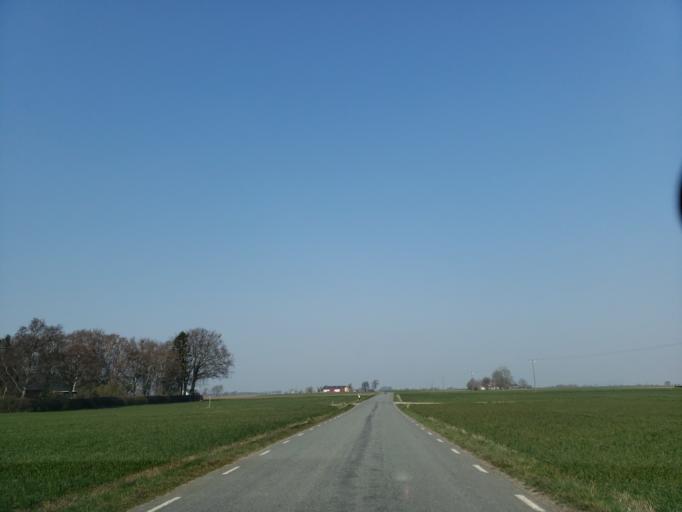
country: SE
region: Skane
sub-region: Simrishamns Kommun
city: Simrishamn
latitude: 55.4521
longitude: 14.2154
